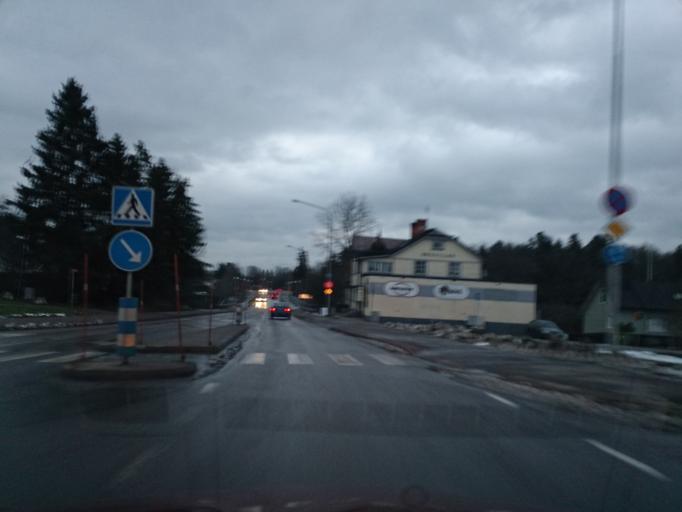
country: SE
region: OEstergoetland
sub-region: Linkopings Kommun
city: Sturefors
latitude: 58.3743
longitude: 15.7101
